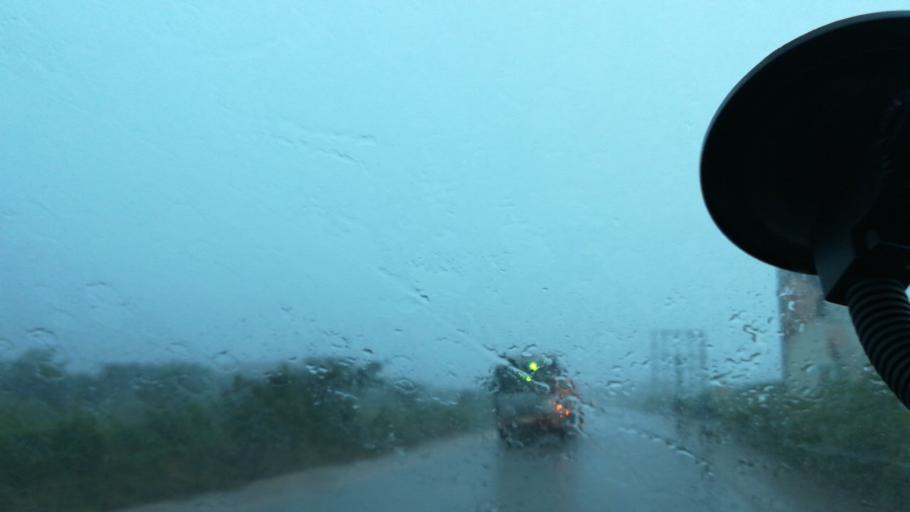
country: CD
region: Katanga
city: Lubumbashi
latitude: -11.5941
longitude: 27.4982
